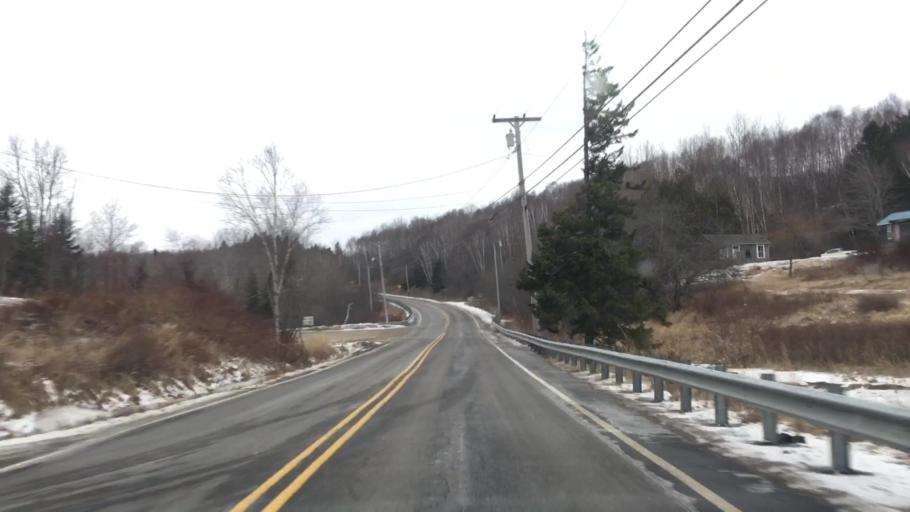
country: US
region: Maine
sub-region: Washington County
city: Machiasport
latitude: 44.7129
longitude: -67.3741
